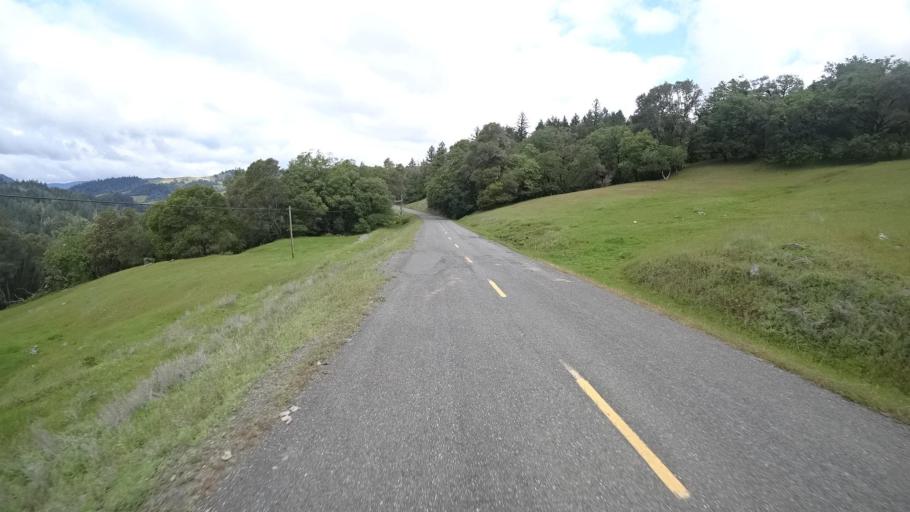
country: US
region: California
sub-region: Humboldt County
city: Redway
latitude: 40.2311
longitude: -123.6160
